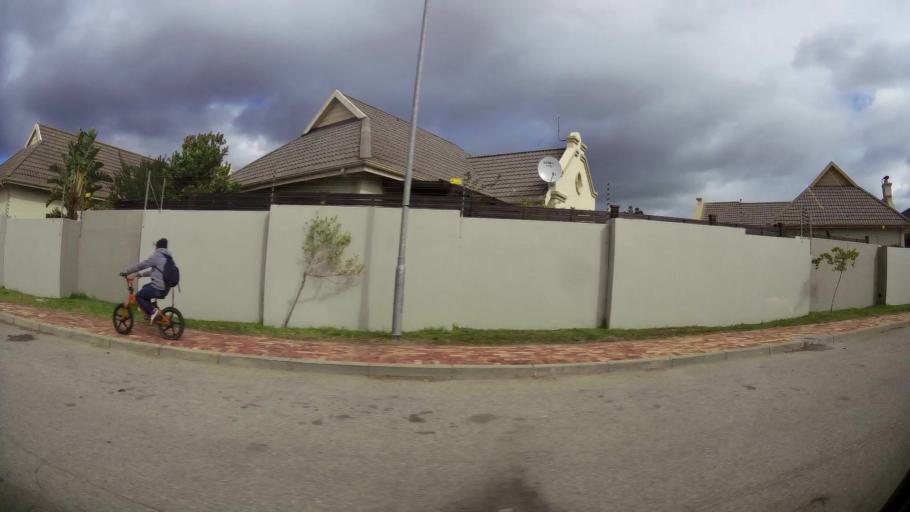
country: ZA
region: Western Cape
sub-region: Eden District Municipality
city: George
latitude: -33.9839
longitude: 22.4977
